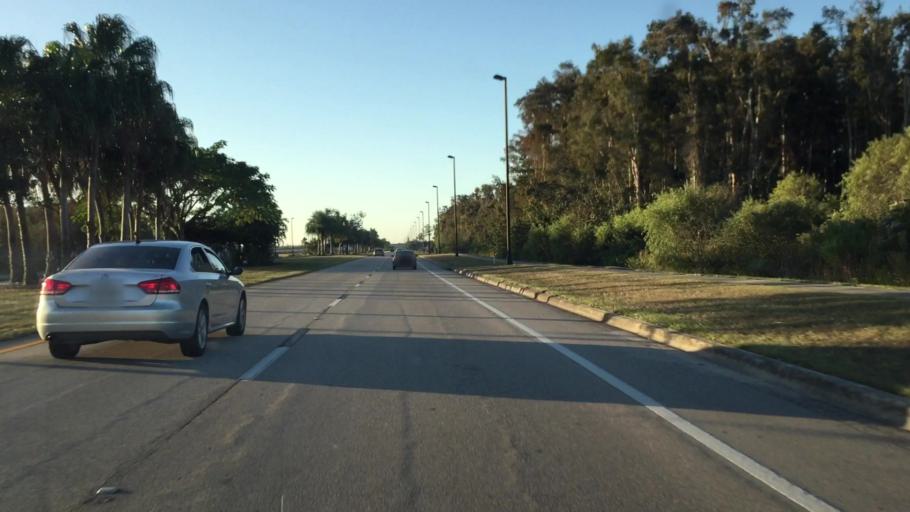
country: US
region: Florida
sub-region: Lee County
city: Three Oaks
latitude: 26.5218
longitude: -81.7856
